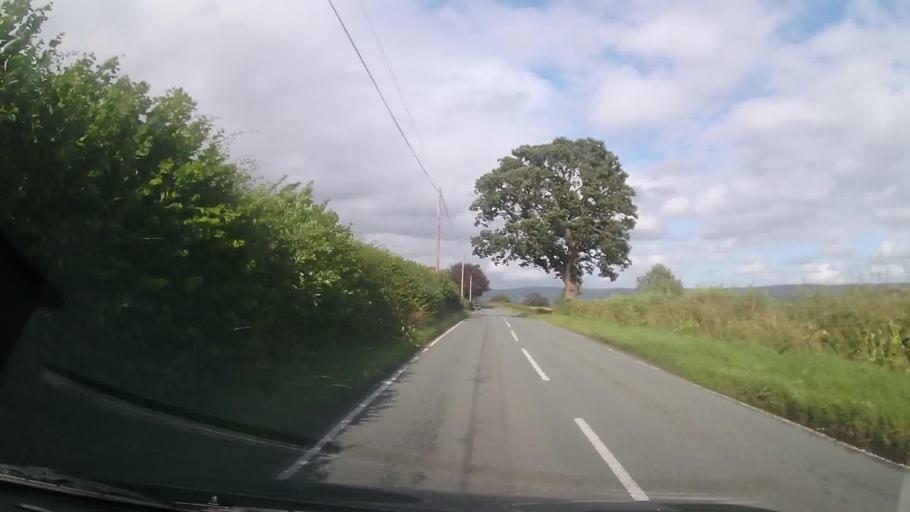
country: GB
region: England
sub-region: Shropshire
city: Lydham
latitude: 52.5004
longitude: -2.9749
